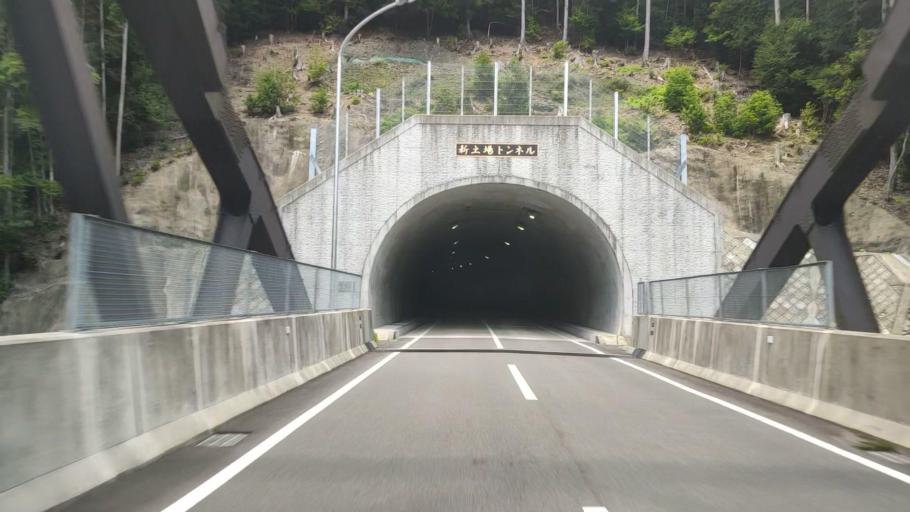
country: JP
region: Mie
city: Owase
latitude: 34.0033
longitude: 136.0095
